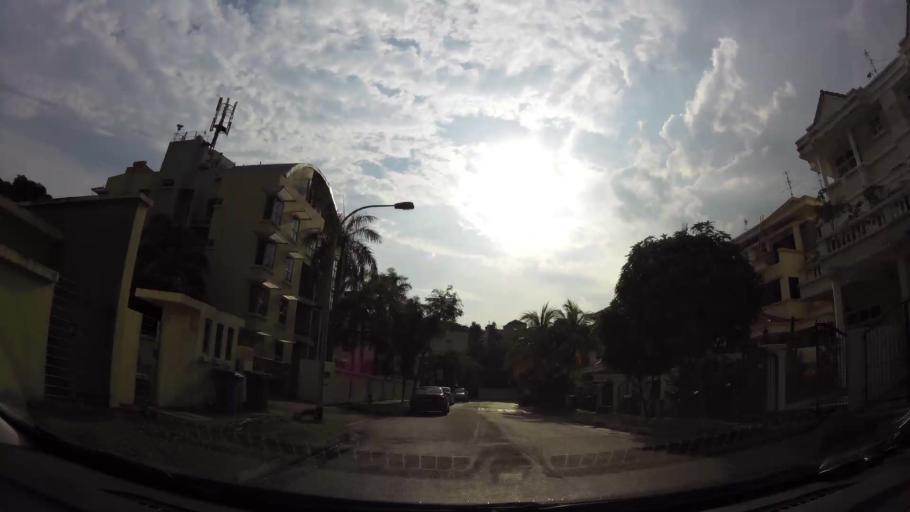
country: SG
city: Singapore
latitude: 1.3211
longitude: 103.9571
